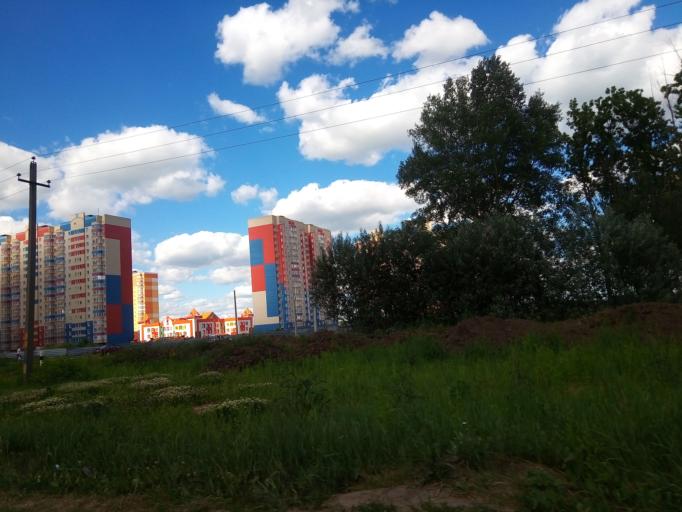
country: RU
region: Kursk
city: Kursk
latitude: 51.8127
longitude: 36.1639
